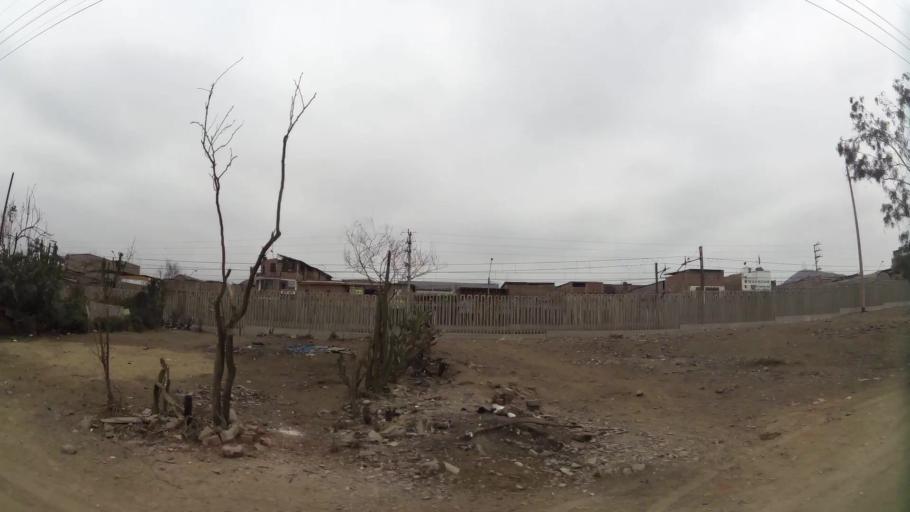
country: PE
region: Lima
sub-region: Lima
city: Surco
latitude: -12.2037
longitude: -76.9358
